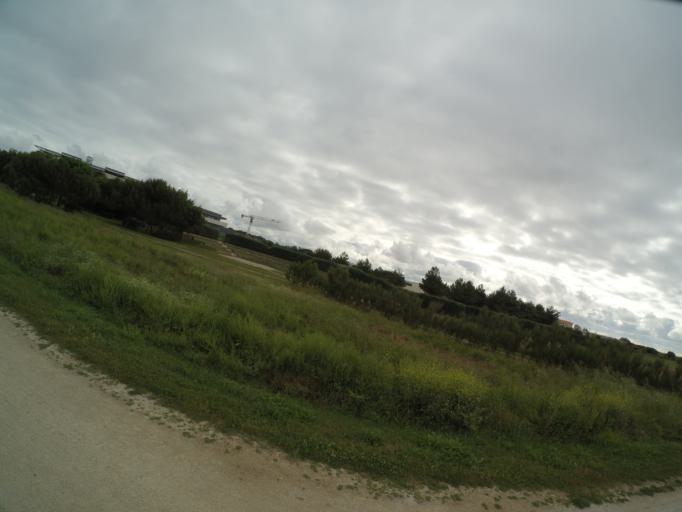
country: FR
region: Poitou-Charentes
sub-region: Departement de la Charente-Maritime
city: La Rochelle
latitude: 46.1358
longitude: -1.1522
